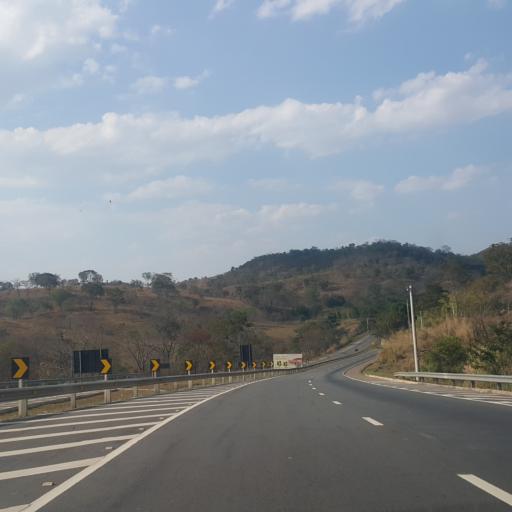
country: BR
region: Goias
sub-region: Abadiania
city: Abadiania
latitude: -16.1137
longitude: -48.5882
